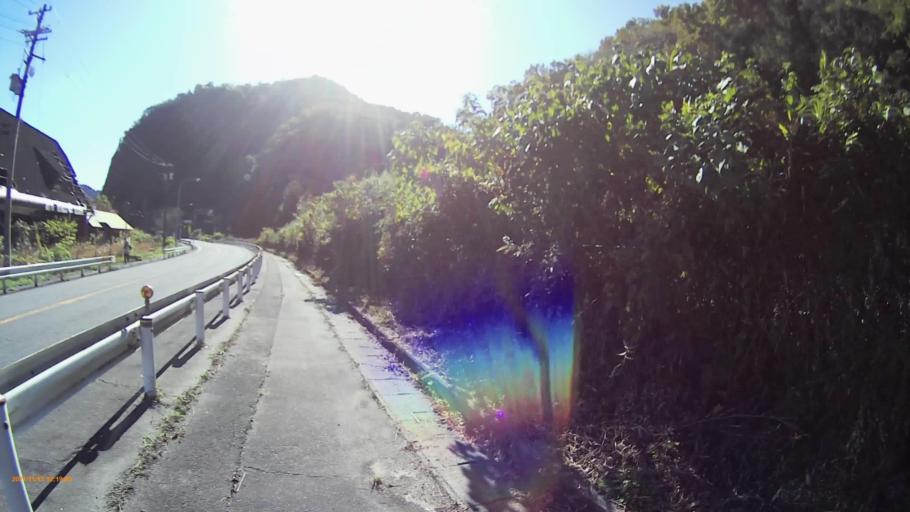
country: JP
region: Gifu
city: Inuyama
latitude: 35.4154
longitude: 136.9593
